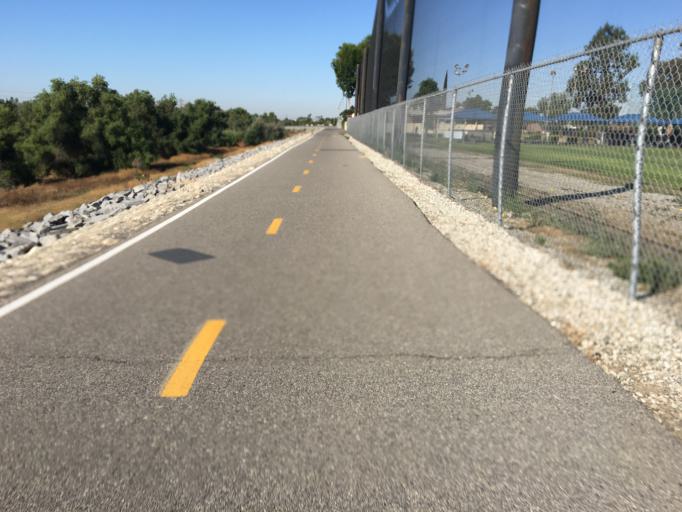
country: US
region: California
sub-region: Los Angeles County
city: South El Monte
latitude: 34.0197
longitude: -118.0579
